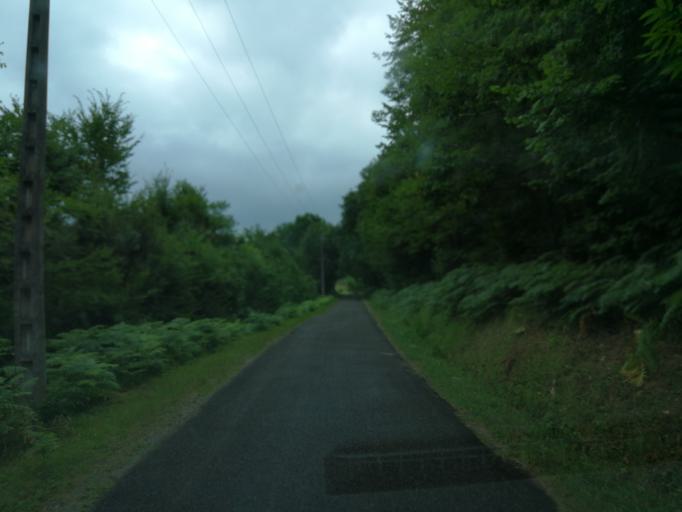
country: FR
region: Aquitaine
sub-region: Departement du Lot-et-Garonne
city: Montayral
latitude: 44.5528
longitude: 1.0735
